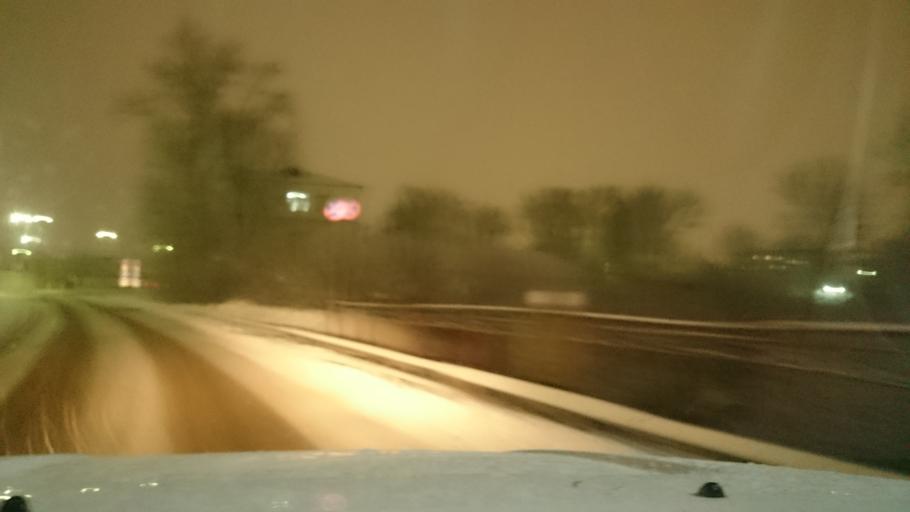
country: RU
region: Tula
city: Tula
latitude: 54.1925
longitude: 37.5737
